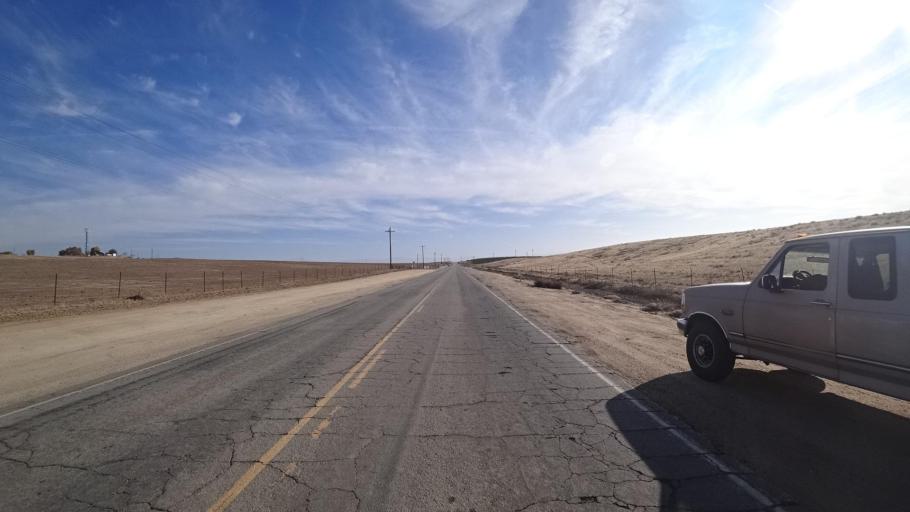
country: US
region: California
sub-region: Kern County
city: McFarland
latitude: 35.6025
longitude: -119.0865
